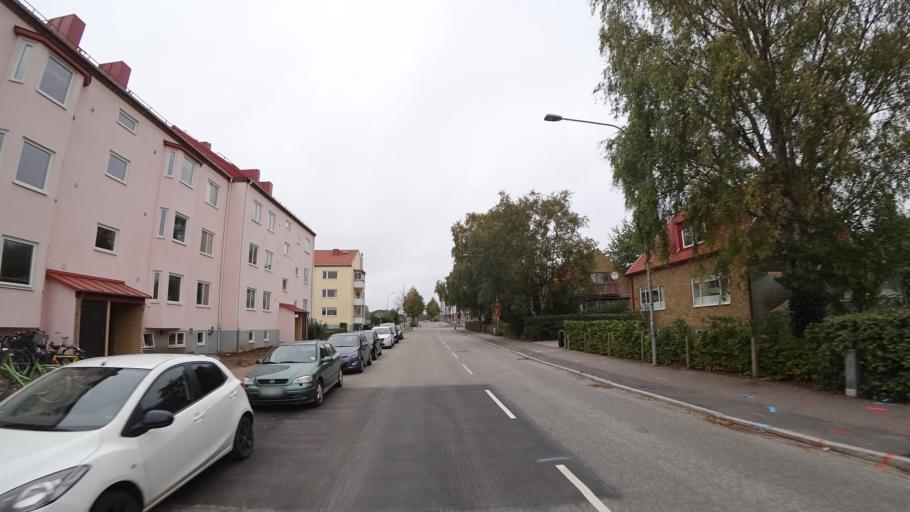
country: SE
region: Skane
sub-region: Kavlinge Kommun
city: Kaevlinge
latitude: 55.7923
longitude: 13.1188
